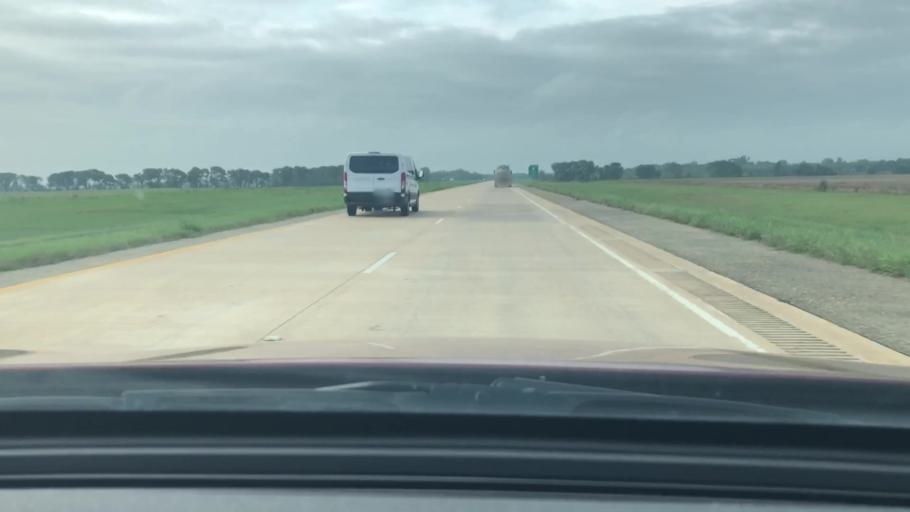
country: US
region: Louisiana
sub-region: Caddo Parish
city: Vivian
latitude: 32.8732
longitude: -93.8605
